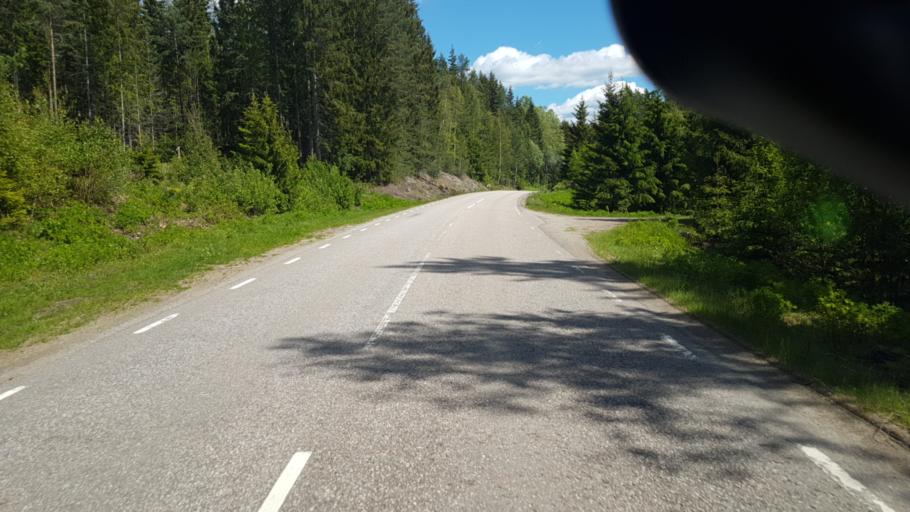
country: SE
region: Vaermland
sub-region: Arvika Kommun
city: Arvika
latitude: 59.6257
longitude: 12.8663
